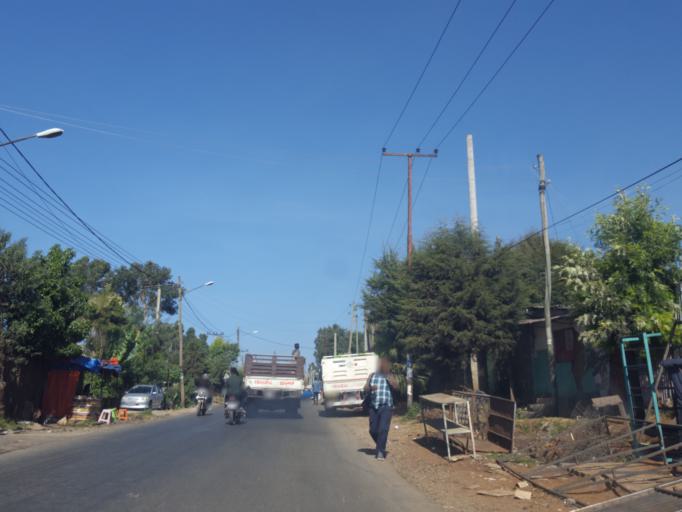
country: ET
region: Adis Abeba
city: Addis Ababa
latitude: 9.0540
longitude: 38.7337
